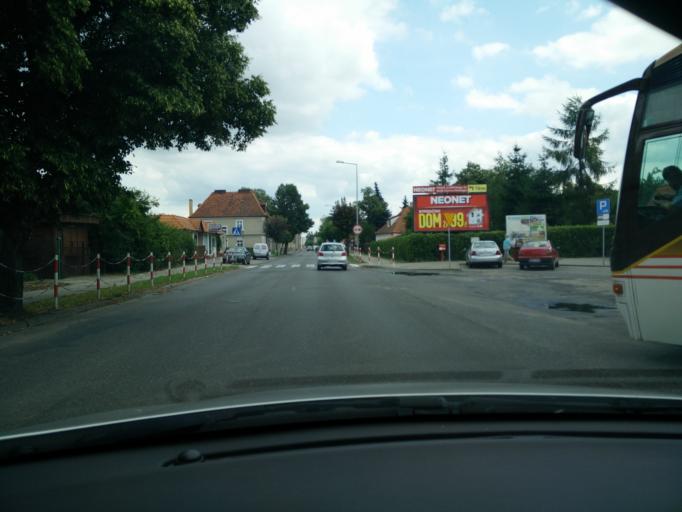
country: PL
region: Greater Poland Voivodeship
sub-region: Powiat sredzki
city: Sroda Wielkopolska
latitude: 52.2283
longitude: 17.2675
